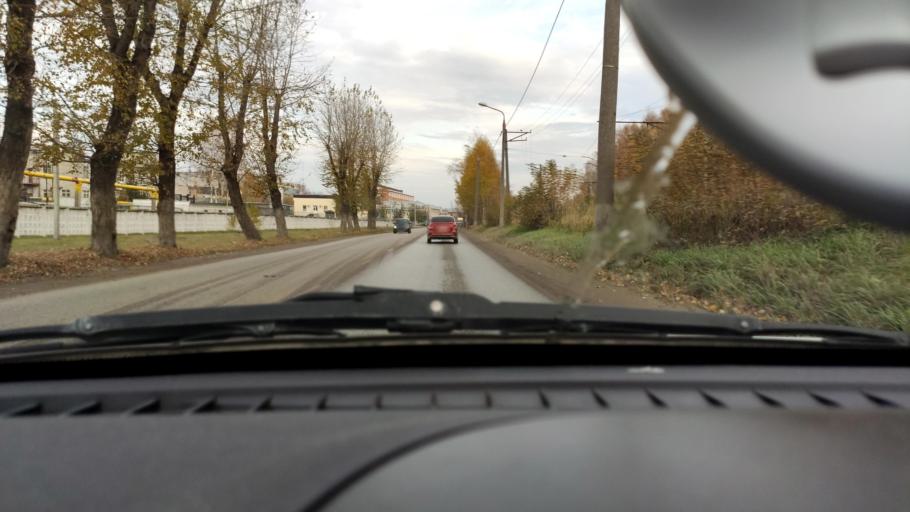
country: RU
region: Perm
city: Perm
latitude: 58.0900
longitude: 56.3534
